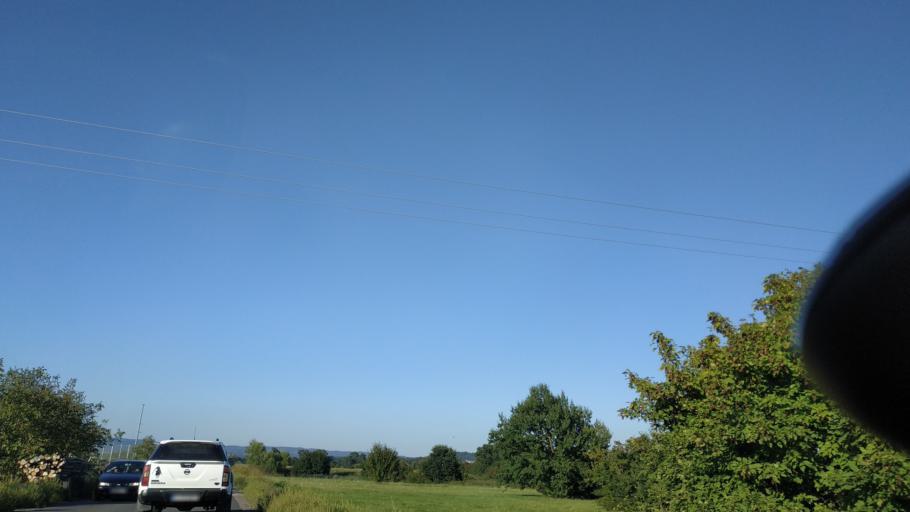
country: RS
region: Central Serbia
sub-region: Rasinski Okrug
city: Krusevac
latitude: 43.5180
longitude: 21.3294
